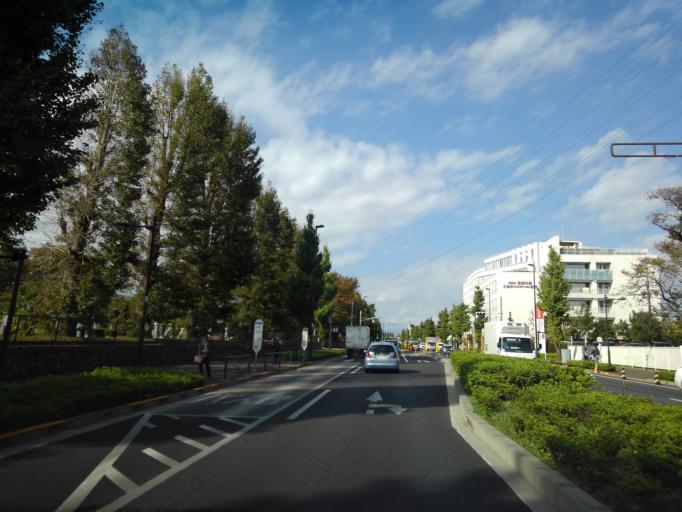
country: JP
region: Tokyo
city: Kokubunji
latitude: 35.6883
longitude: 139.5136
